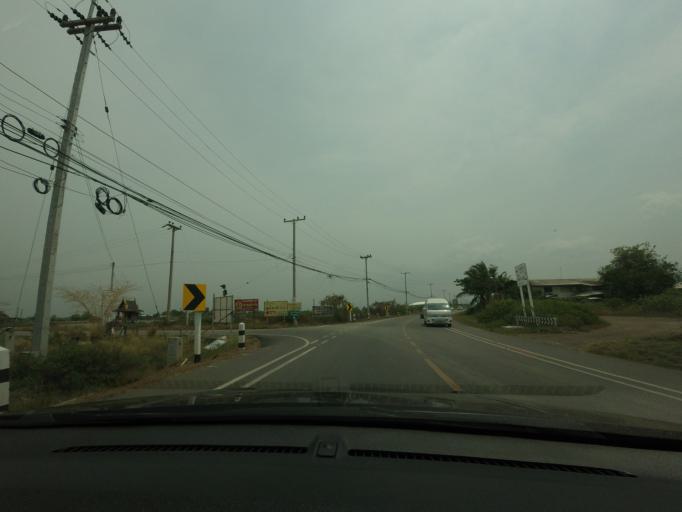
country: TH
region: Ratchaburi
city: Pak Tho
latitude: 13.3203
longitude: 99.9237
